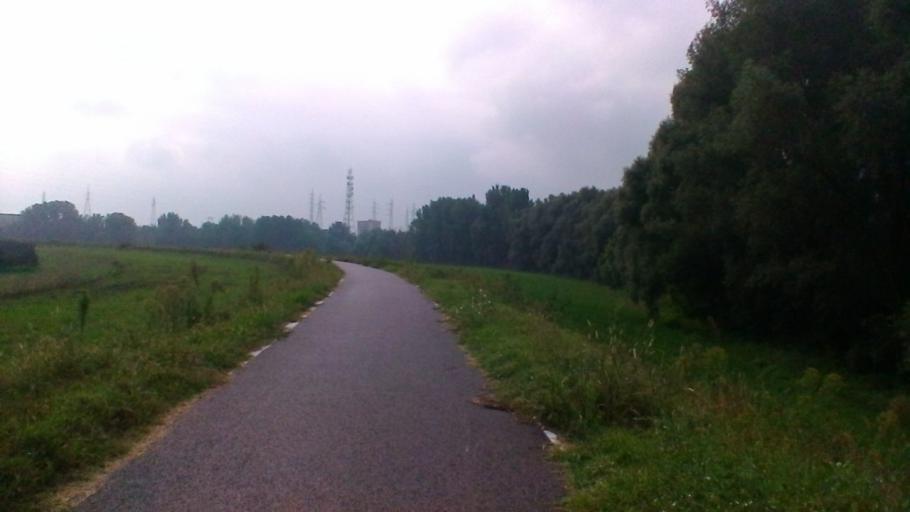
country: IT
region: Veneto
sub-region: Provincia di Verona
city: San Giovanni Lupatoto
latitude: 45.3984
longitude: 11.0324
